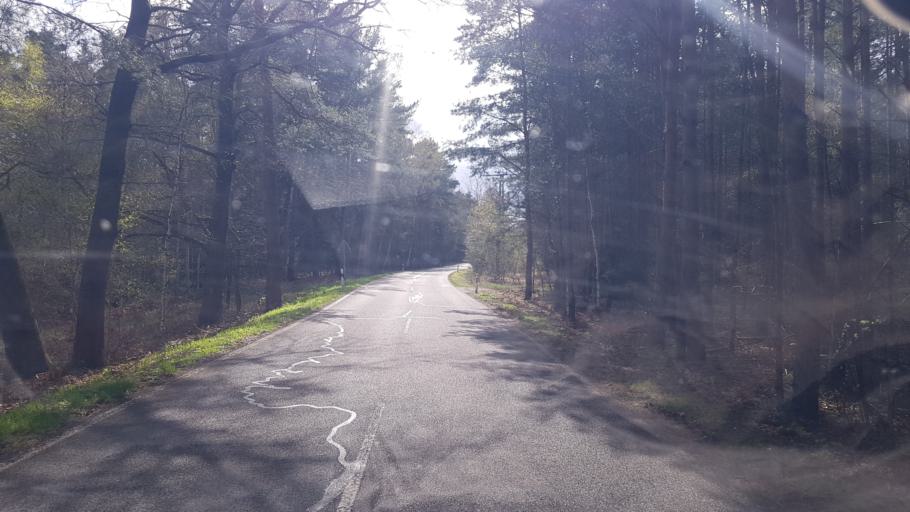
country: DE
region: Brandenburg
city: Crinitz
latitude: 51.7186
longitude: 13.8183
